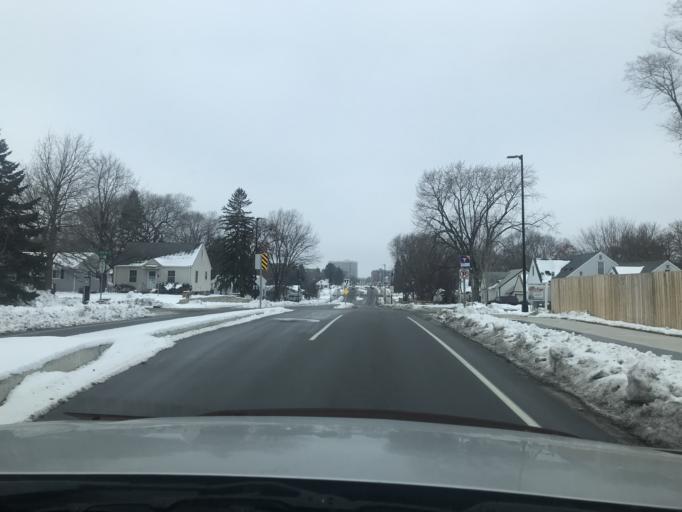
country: US
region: Minnesota
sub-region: Hennepin County
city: Richfield
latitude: 44.8835
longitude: -93.2724
